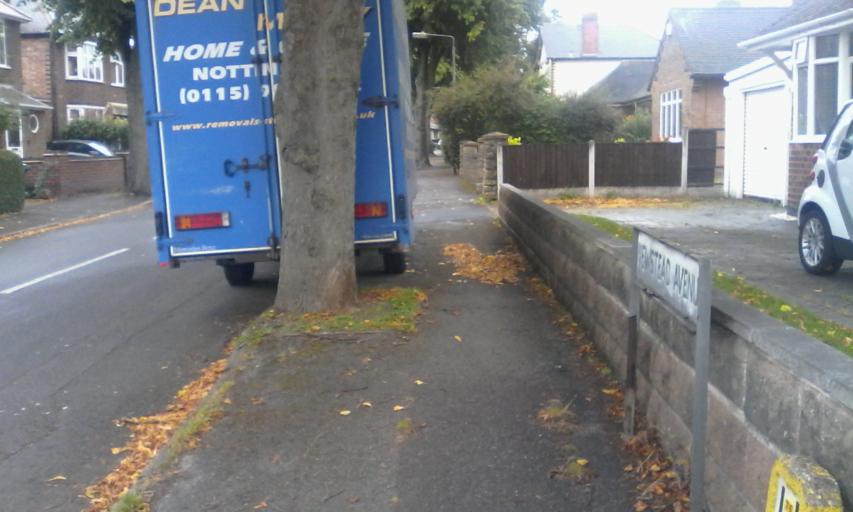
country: GB
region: England
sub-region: Nottinghamshire
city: Arnold
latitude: 52.9788
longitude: -1.1055
